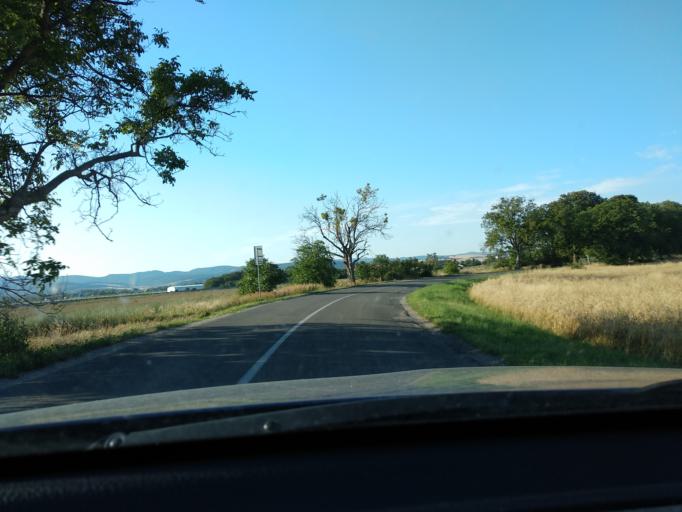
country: SK
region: Trenciansky
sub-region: Okres Trencin
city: Trencin
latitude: 48.8638
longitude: 18.0171
